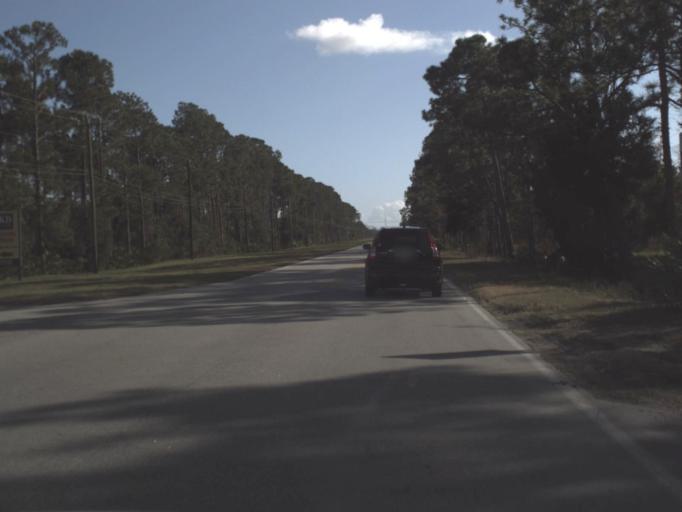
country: US
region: Florida
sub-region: Volusia County
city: Holly Hill
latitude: 29.2371
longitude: -81.0983
